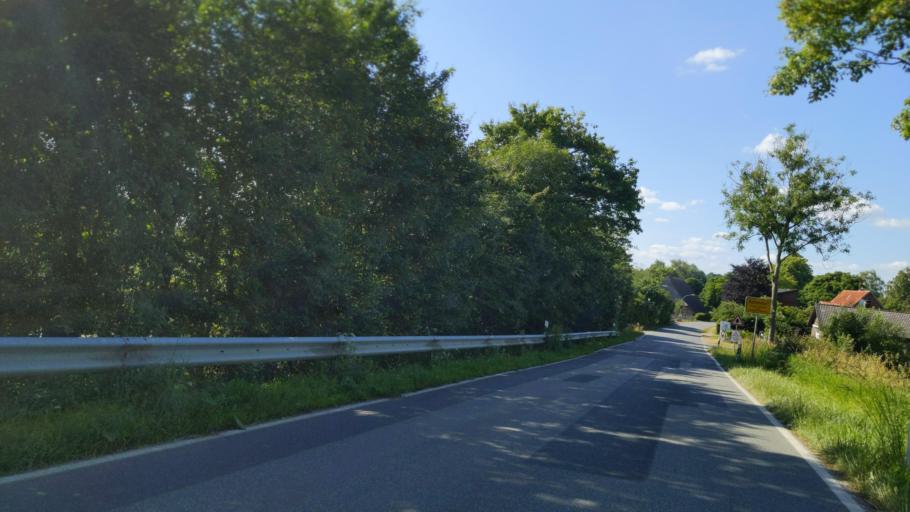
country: DE
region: Schleswig-Holstein
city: Goldenitz
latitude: 53.7124
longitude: 10.6489
